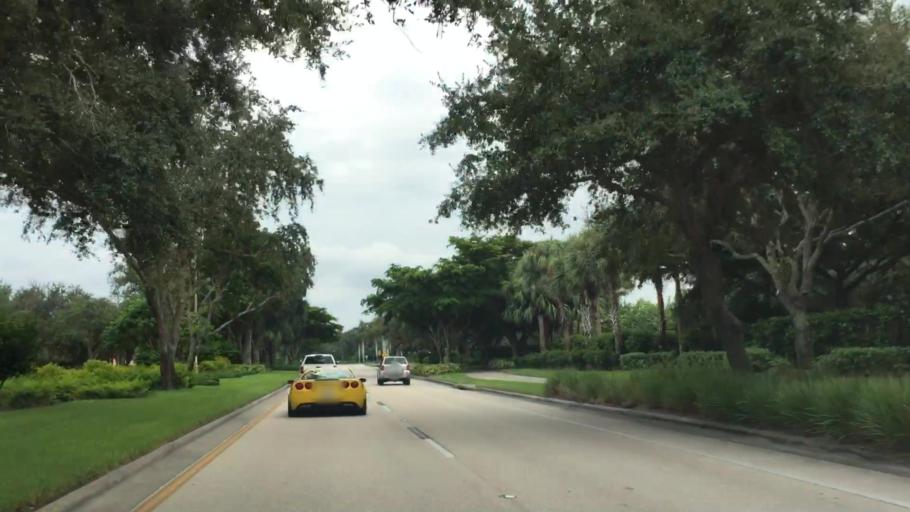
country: US
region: Florida
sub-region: Lee County
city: Estero
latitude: 26.3974
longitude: -81.7971
